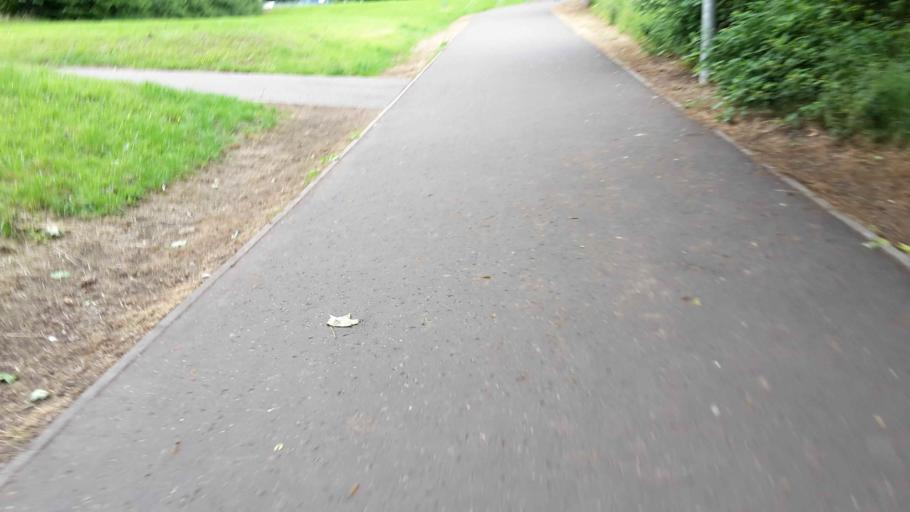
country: GB
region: Scotland
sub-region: South Lanarkshire
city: Uddingston
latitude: 55.8185
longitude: -4.0735
